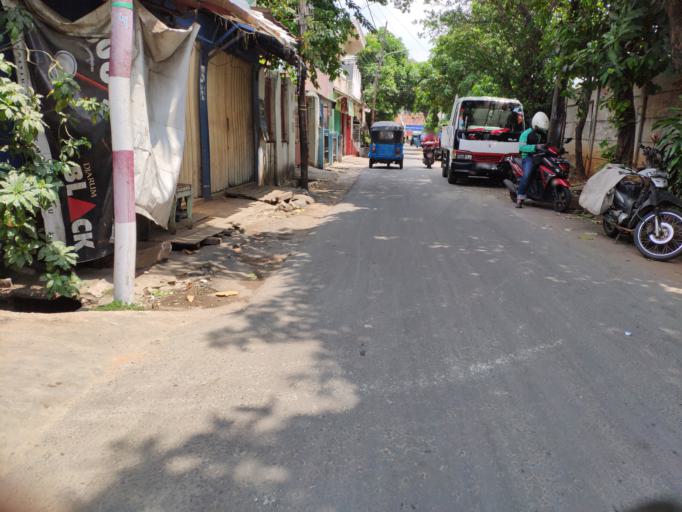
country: ID
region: Jakarta Raya
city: Jakarta
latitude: -6.2146
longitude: 106.8717
